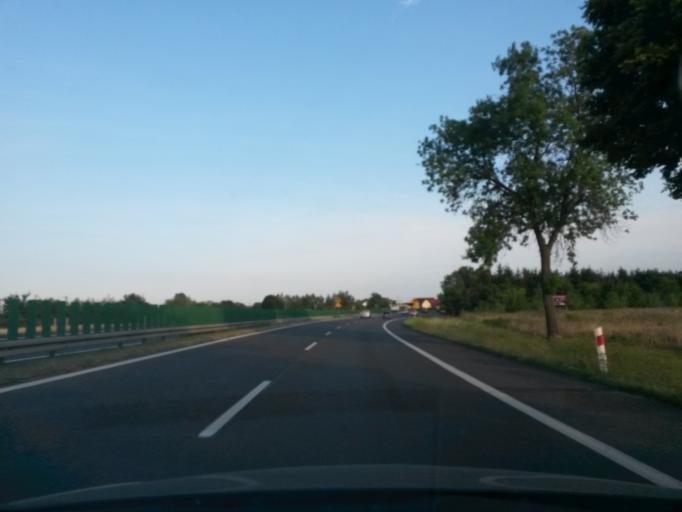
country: PL
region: Masovian Voivodeship
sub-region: Powiat plonski
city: Zaluski
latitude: 52.4793
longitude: 20.5609
